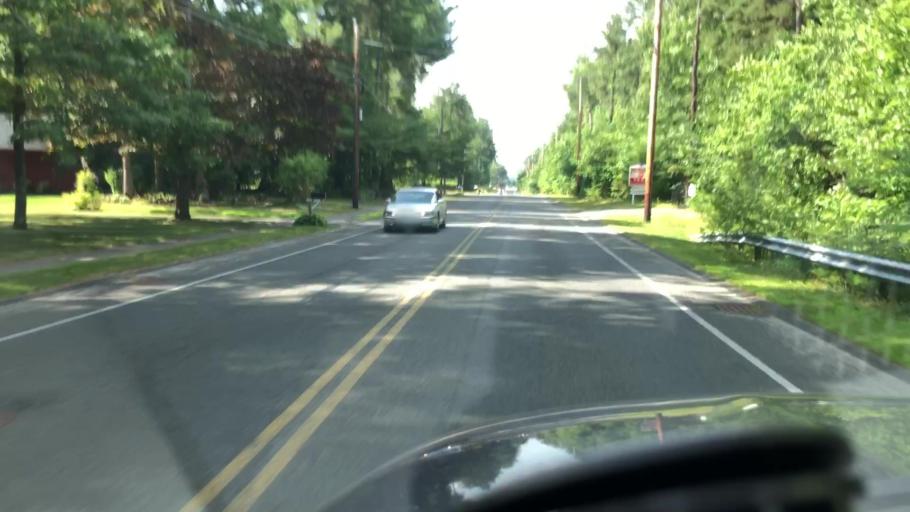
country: US
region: Massachusetts
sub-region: Hampshire County
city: Southampton
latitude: 42.1979
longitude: -72.6878
